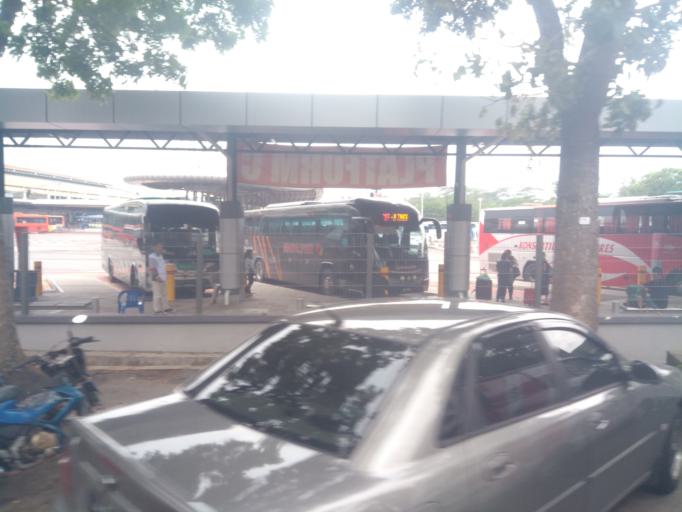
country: MY
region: Johor
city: Johor Bahru
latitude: 1.4948
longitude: 103.7417
